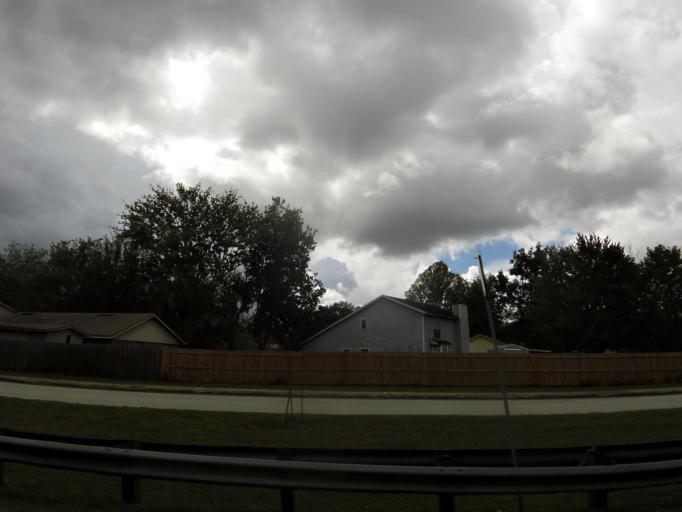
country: US
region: Florida
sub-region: Clay County
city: Lakeside
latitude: 30.1004
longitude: -81.7514
